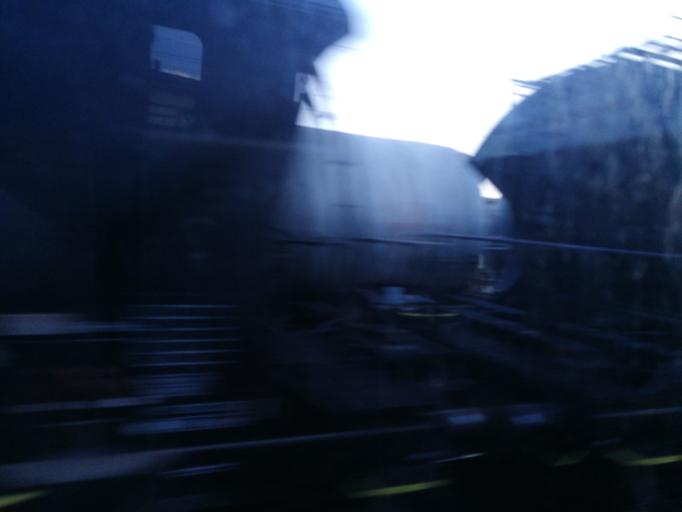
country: RO
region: Ilfov
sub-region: Comuna Chitila
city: Chitila
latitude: 44.5019
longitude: 25.9843
